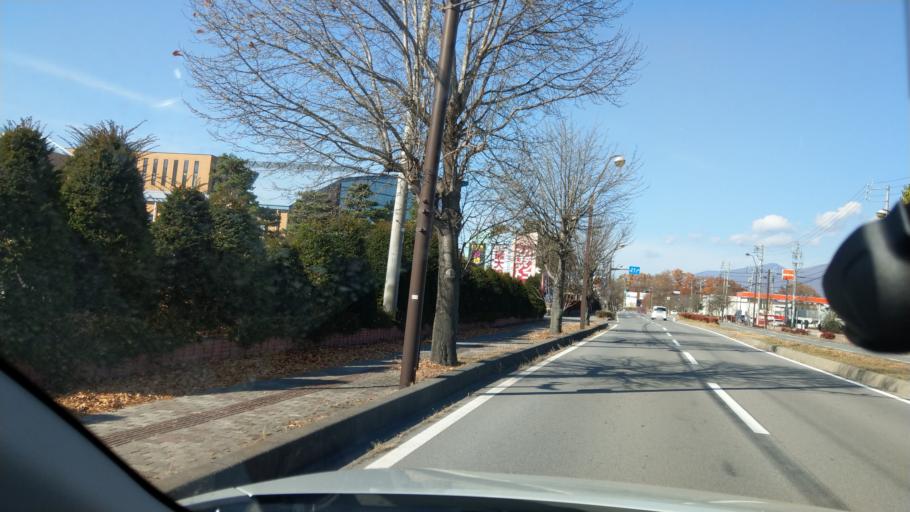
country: JP
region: Nagano
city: Komoro
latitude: 36.2862
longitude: 138.4794
